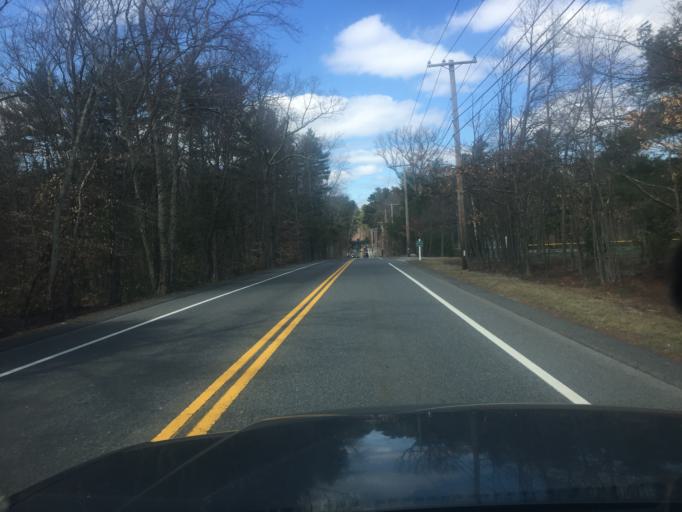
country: US
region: Massachusetts
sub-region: Norfolk County
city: Norfolk
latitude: 42.1034
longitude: -71.3092
